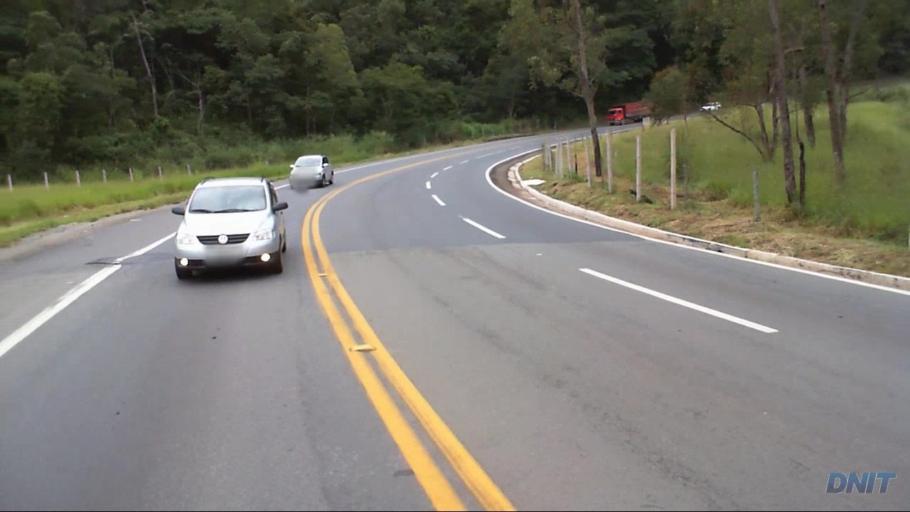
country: BR
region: Minas Gerais
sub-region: Joao Monlevade
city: Joao Monlevade
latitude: -19.8553
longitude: -43.2271
